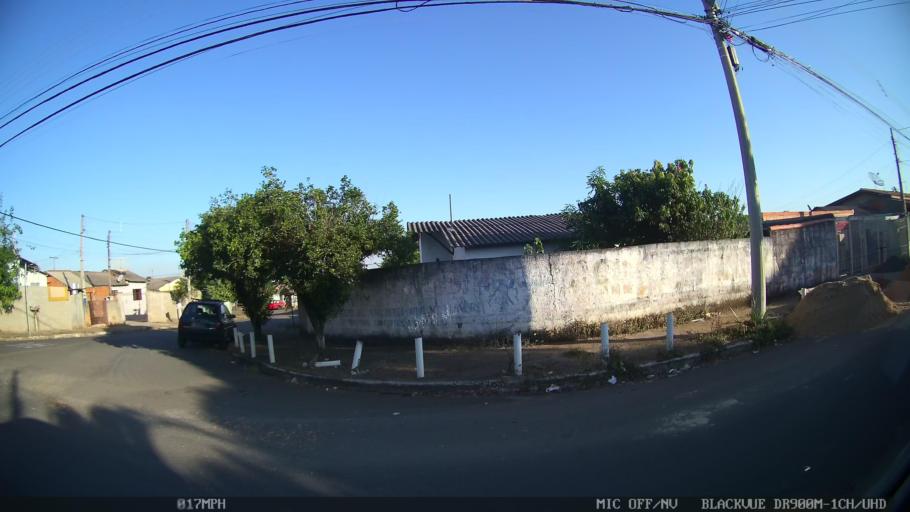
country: BR
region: Sao Paulo
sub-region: Nova Odessa
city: Nova Odessa
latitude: -22.7787
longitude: -47.2817
